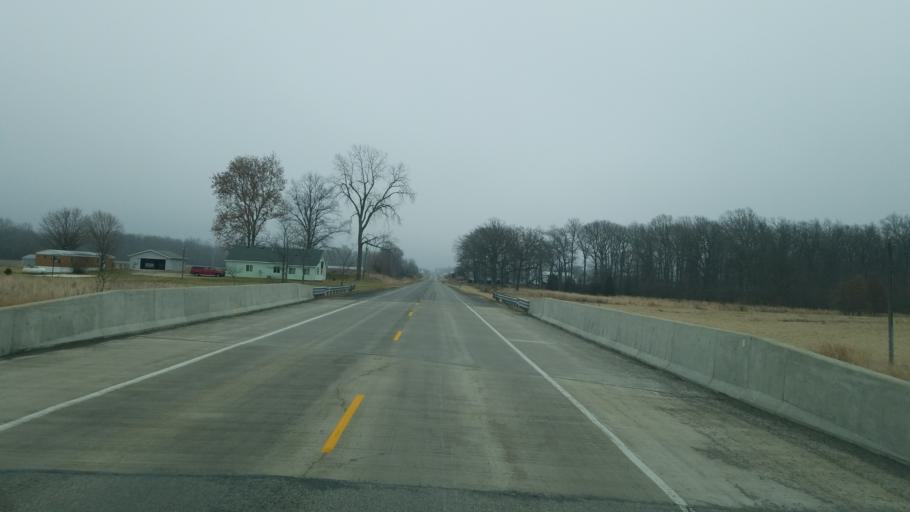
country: US
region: Indiana
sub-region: Adams County
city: Geneva
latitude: 40.5474
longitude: -85.0274
